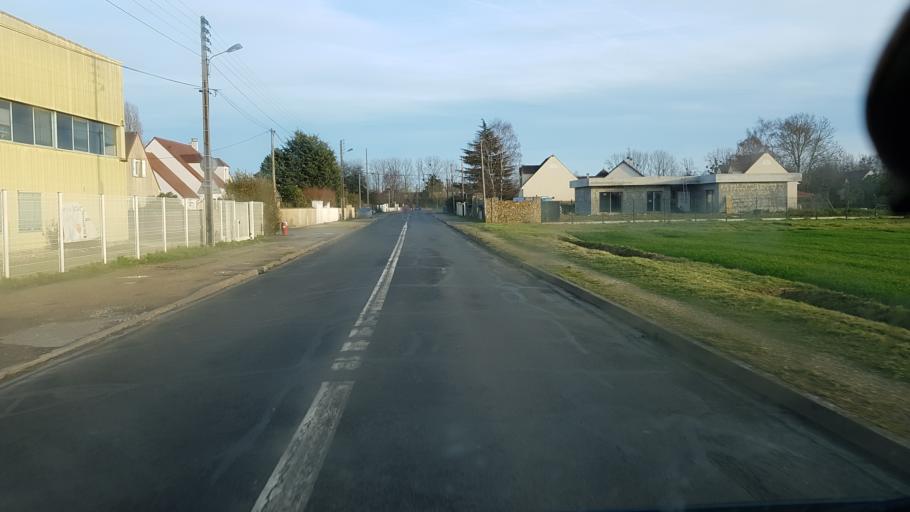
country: FR
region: Ile-de-France
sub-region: Departement des Yvelines
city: Le Perray-en-Yvelines
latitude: 48.6951
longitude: 1.8415
